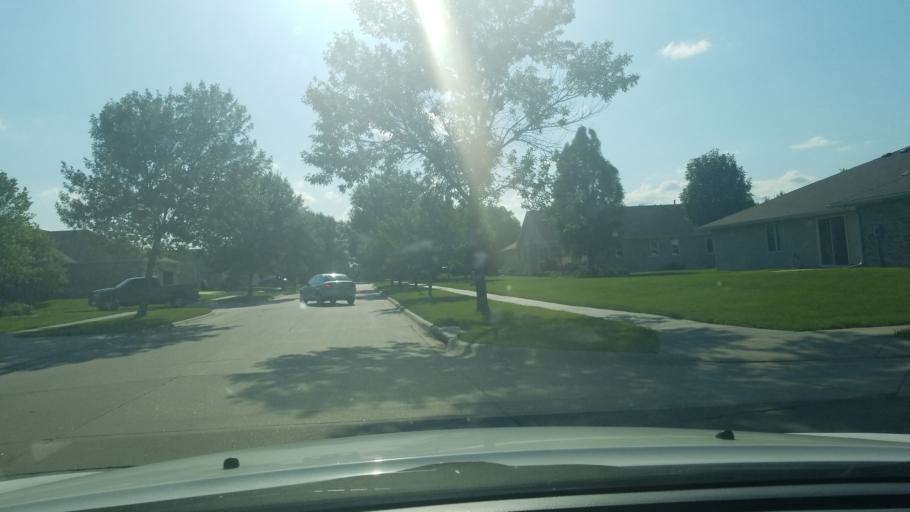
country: US
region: Nebraska
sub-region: Lancaster County
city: Lincoln
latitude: 40.7504
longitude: -96.6099
